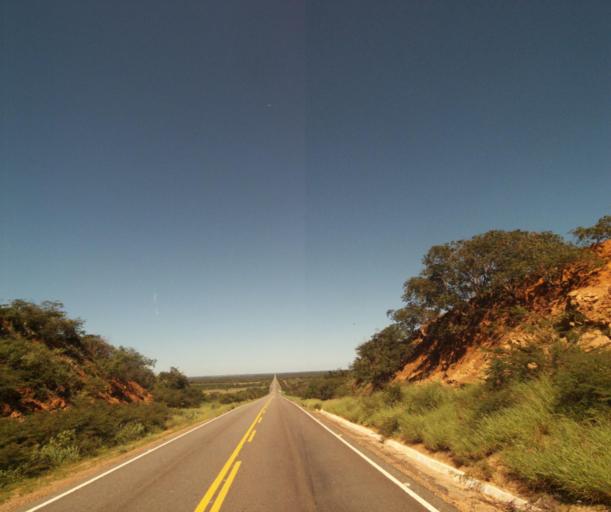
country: BR
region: Bahia
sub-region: Palmas De Monte Alto
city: Palmas de Monte Alto
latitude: -14.2506
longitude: -43.1770
